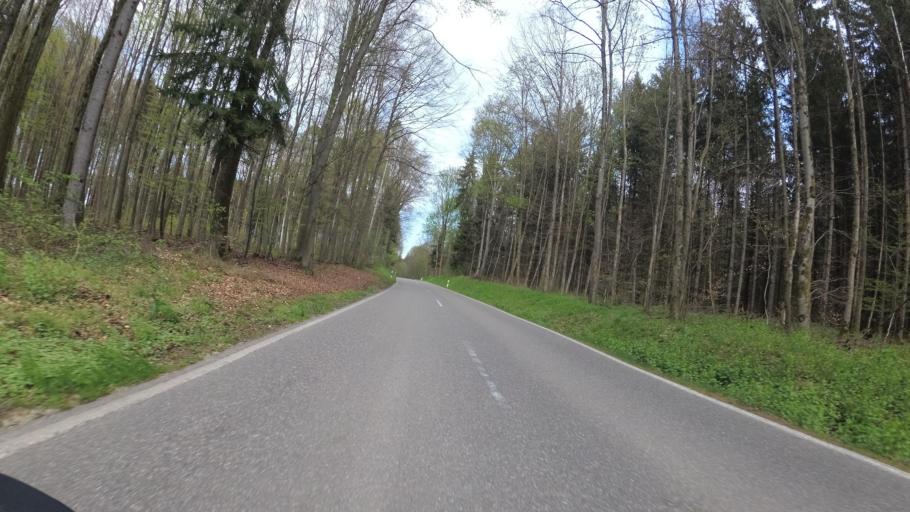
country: DE
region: Baden-Wuerttemberg
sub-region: Regierungsbezirk Stuttgart
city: Neuenstadt am Kocher
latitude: 49.2647
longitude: 9.3570
